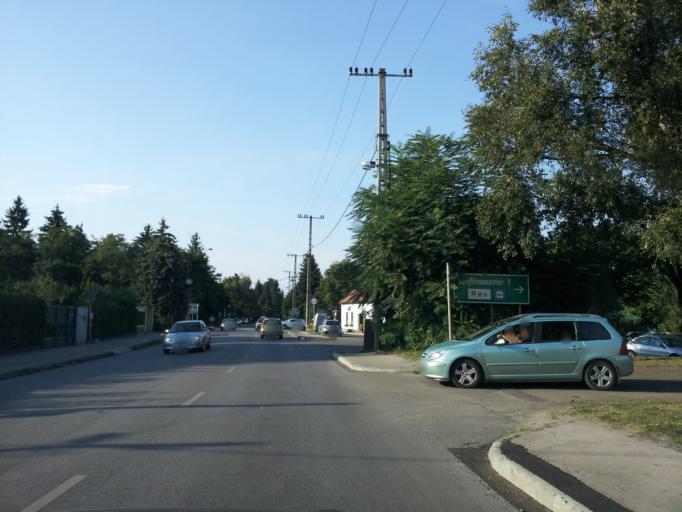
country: HU
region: Pest
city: Leanyfalu
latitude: 47.6938
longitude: 19.0883
